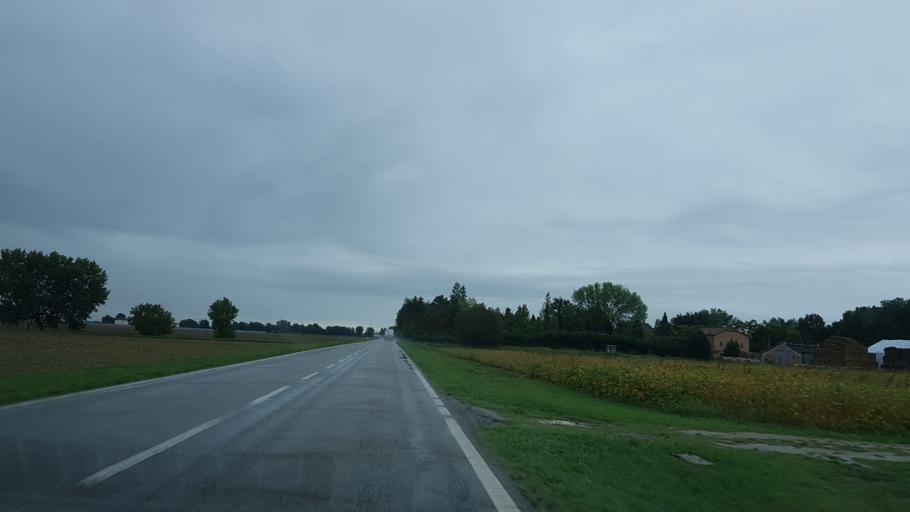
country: IT
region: Emilia-Romagna
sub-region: Provincia di Modena
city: Camposanto
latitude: 44.8026
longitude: 11.1875
